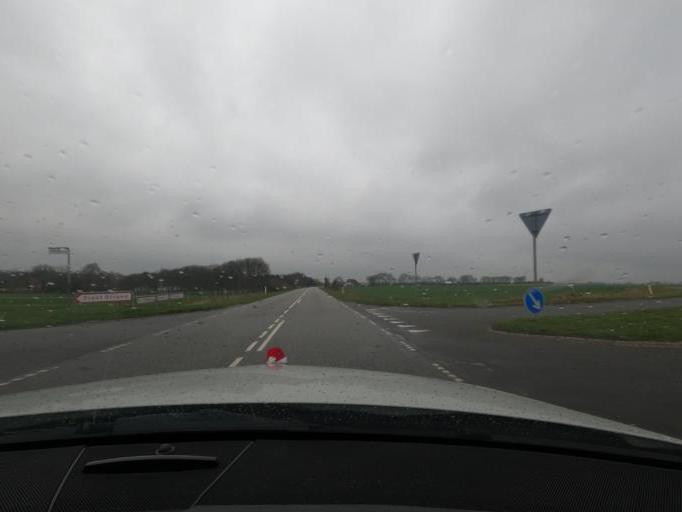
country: DK
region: South Denmark
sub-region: Haderslev Kommune
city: Starup
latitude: 55.2427
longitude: 9.6661
